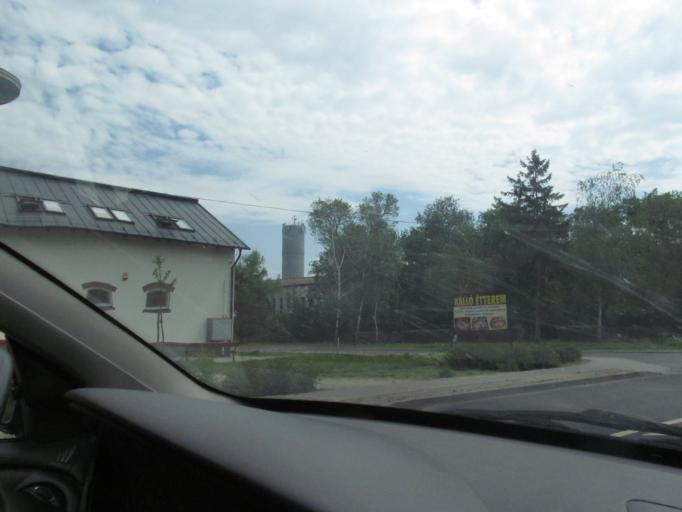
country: HU
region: Szabolcs-Szatmar-Bereg
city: Nagykallo
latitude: 47.8767
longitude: 21.8374
